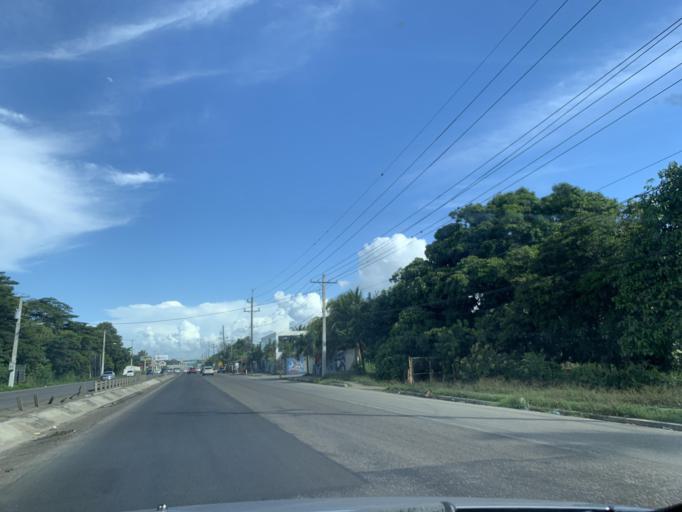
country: DO
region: Santiago
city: Villa Gonzalez
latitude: 19.5218
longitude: -70.7676
